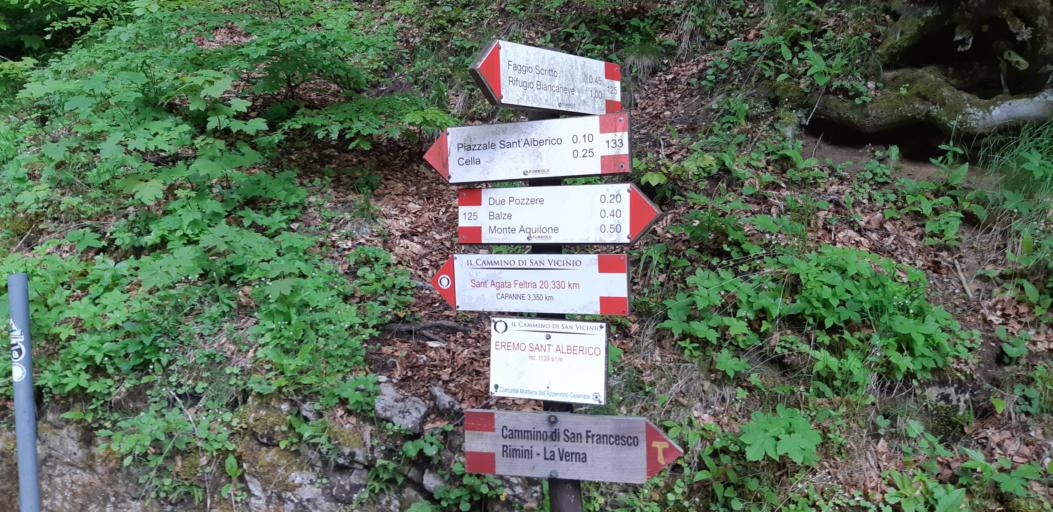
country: IT
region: Emilia-Romagna
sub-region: Provincia di Rimini
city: Casteldelci
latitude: 43.7933
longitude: 12.1000
